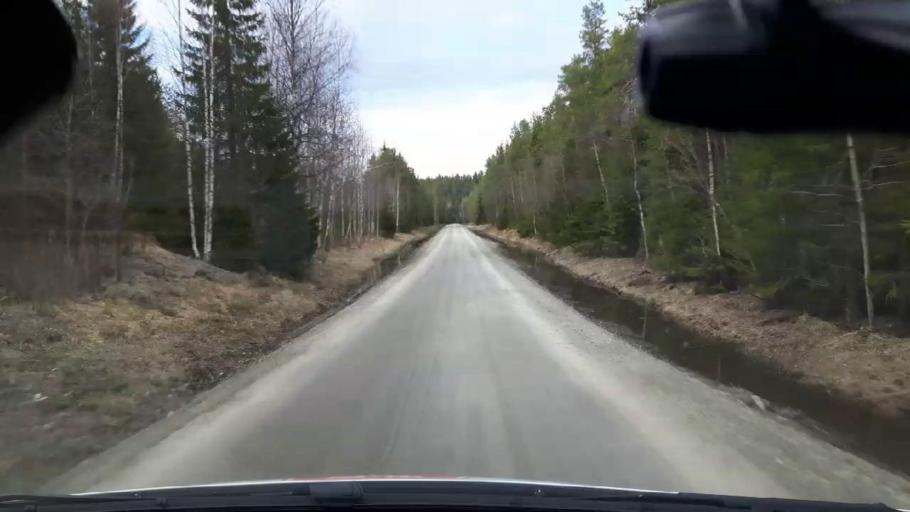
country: SE
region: Jaemtland
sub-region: OEstersunds Kommun
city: Brunflo
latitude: 62.9404
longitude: 14.6655
